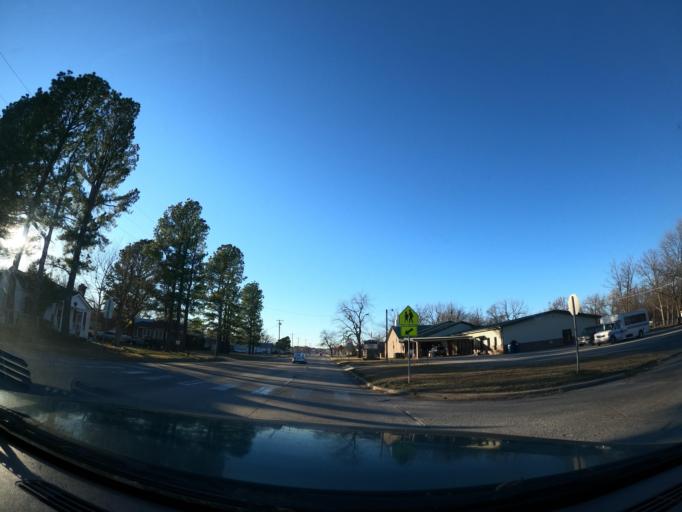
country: US
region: Oklahoma
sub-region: Pittsburg County
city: Hartshorne
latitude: 34.8434
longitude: -95.5508
